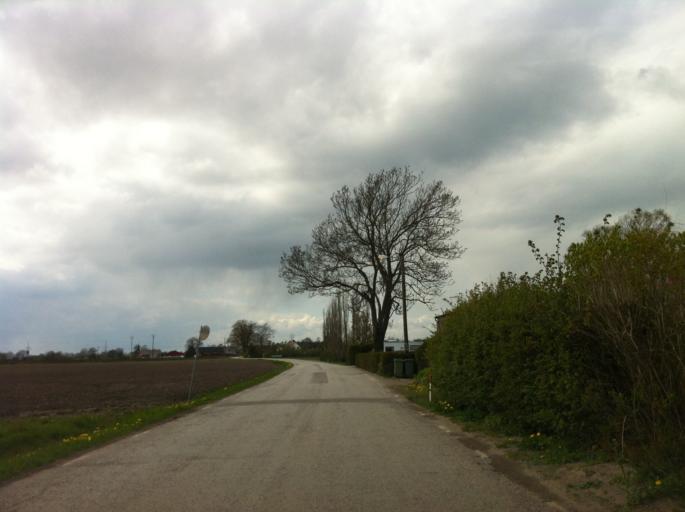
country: SE
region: Skane
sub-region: Kavlinge Kommun
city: Kaevlinge
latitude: 55.8188
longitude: 13.1225
